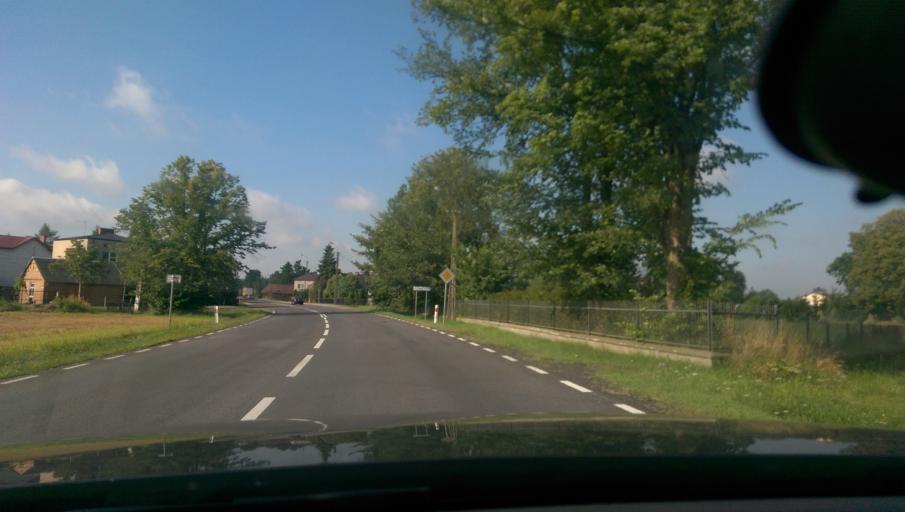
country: PL
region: Masovian Voivodeship
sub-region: Powiat plonski
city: Sochocin
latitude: 52.6913
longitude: 20.4746
